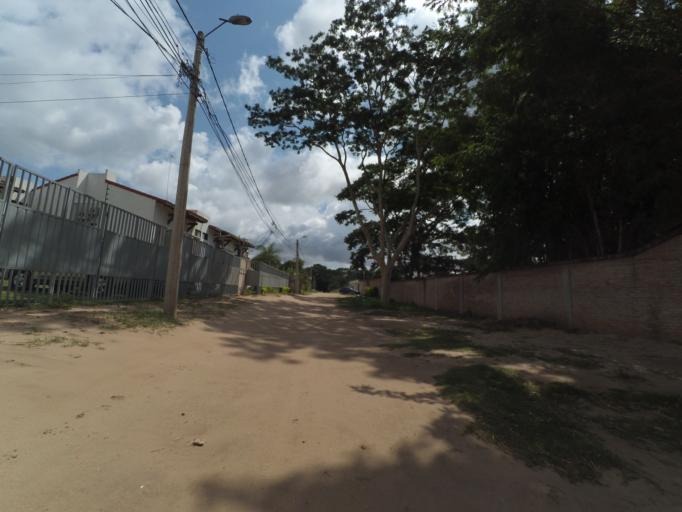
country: BO
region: Santa Cruz
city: Santa Cruz de la Sierra
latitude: -17.8077
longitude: -63.2265
